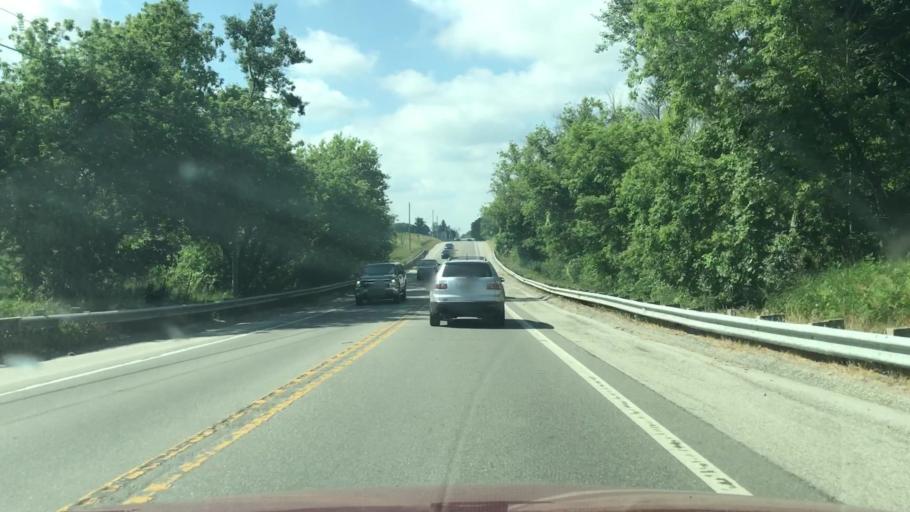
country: US
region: Michigan
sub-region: Kent County
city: Kent City
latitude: 43.3015
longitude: -85.8106
